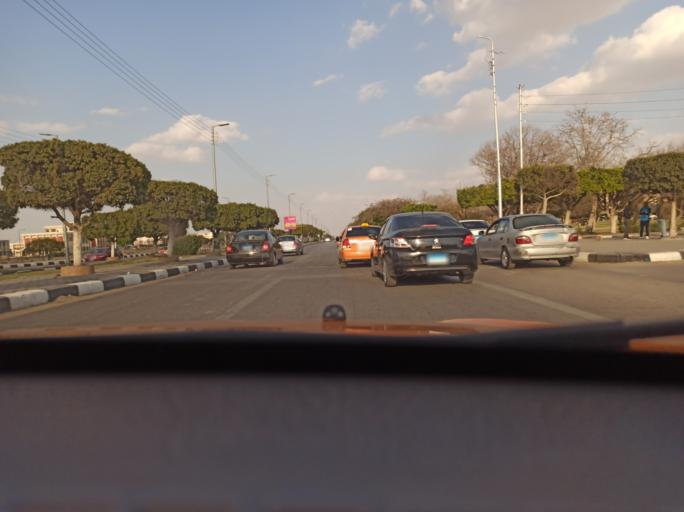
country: EG
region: Al Isma'iliyah
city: Ismailia
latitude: 30.6190
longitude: 32.2743
